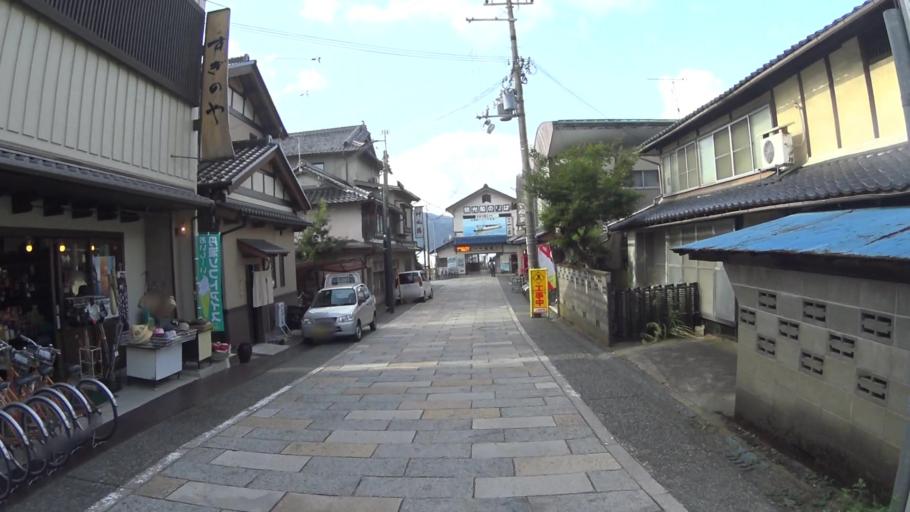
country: JP
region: Kyoto
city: Miyazu
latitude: 35.5812
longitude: 135.1966
